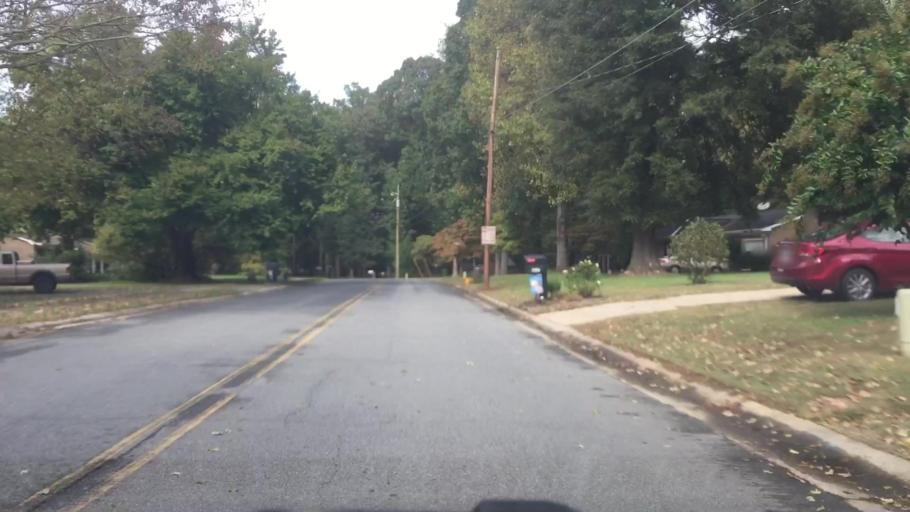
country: US
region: North Carolina
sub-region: Iredell County
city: Mooresville
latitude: 35.5617
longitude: -80.8007
